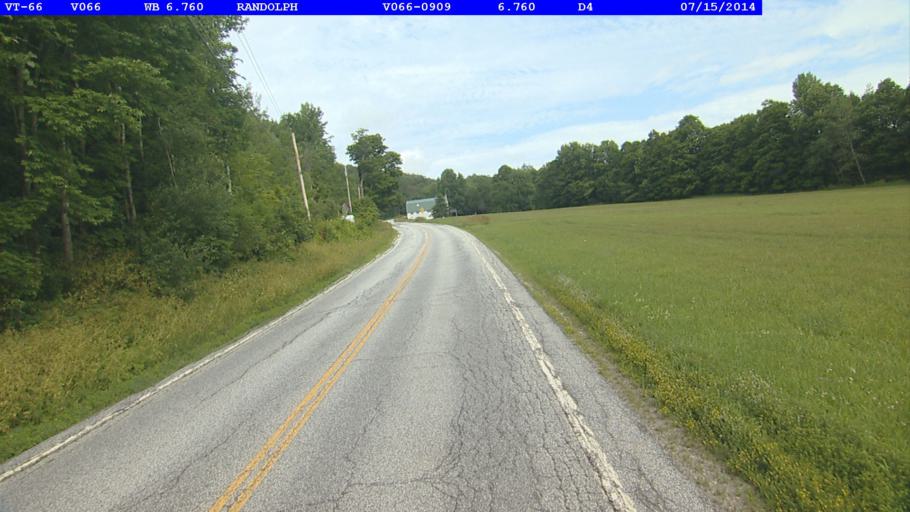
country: US
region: Vermont
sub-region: Orange County
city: Randolph
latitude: 43.9496
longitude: -72.5629
